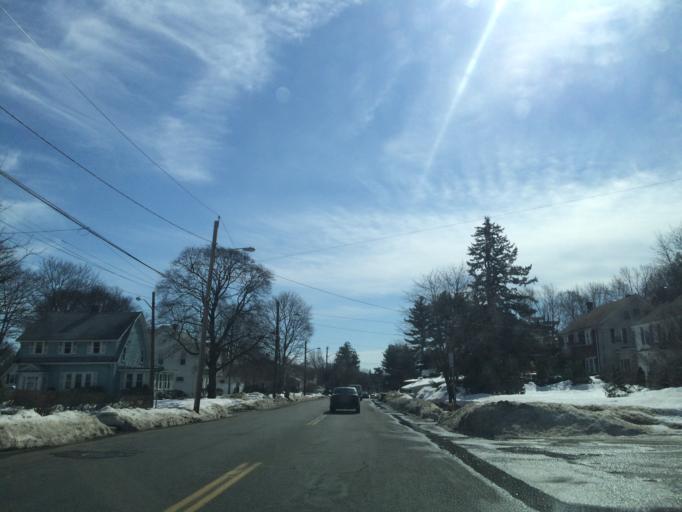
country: US
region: Massachusetts
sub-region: Middlesex County
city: Medford
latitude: 42.4256
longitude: -71.1234
